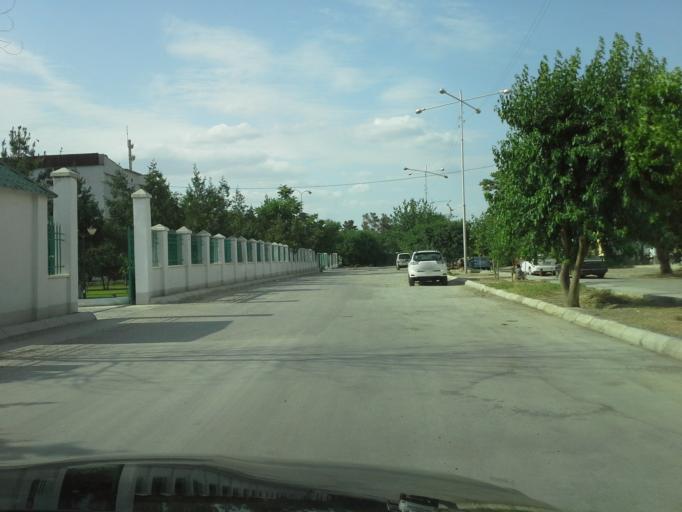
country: TM
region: Ahal
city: Ashgabat
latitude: 37.9565
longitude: 58.3423
